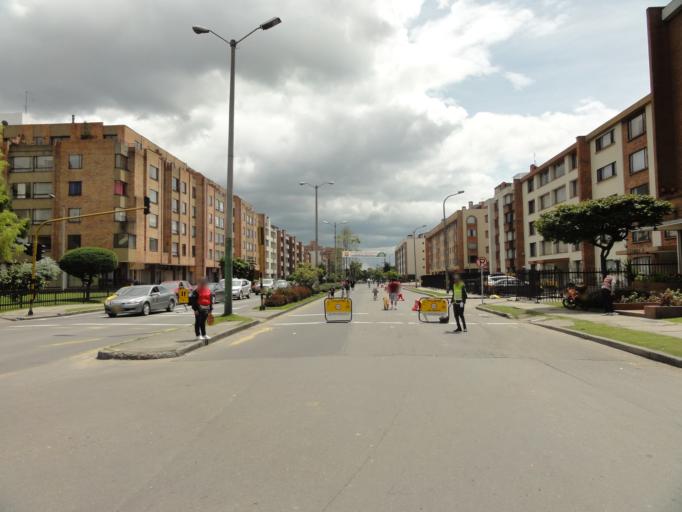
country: CO
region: Bogota D.C.
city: Barrio San Luis
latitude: 4.7008
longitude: -74.0623
